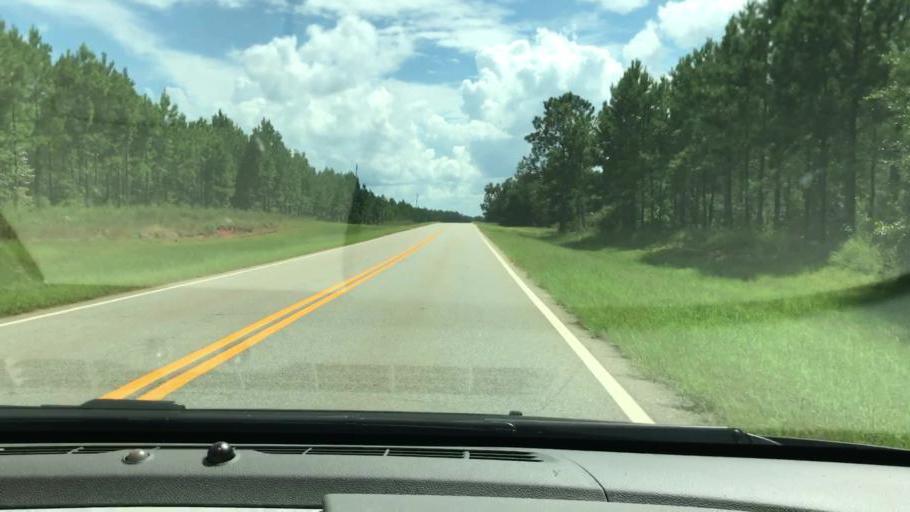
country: US
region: Georgia
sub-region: Quitman County
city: Georgetown
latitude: 31.9193
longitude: -85.0595
